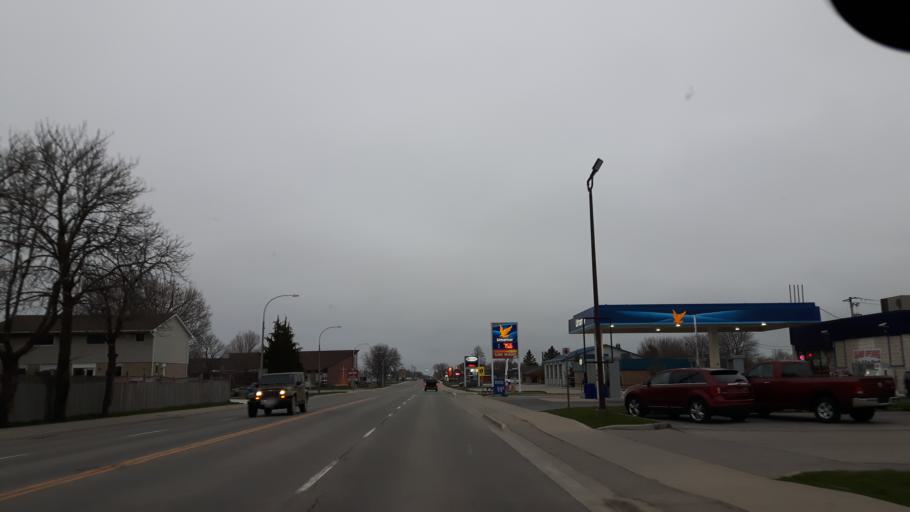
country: CA
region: Ontario
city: Goderich
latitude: 43.7344
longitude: -81.7060
